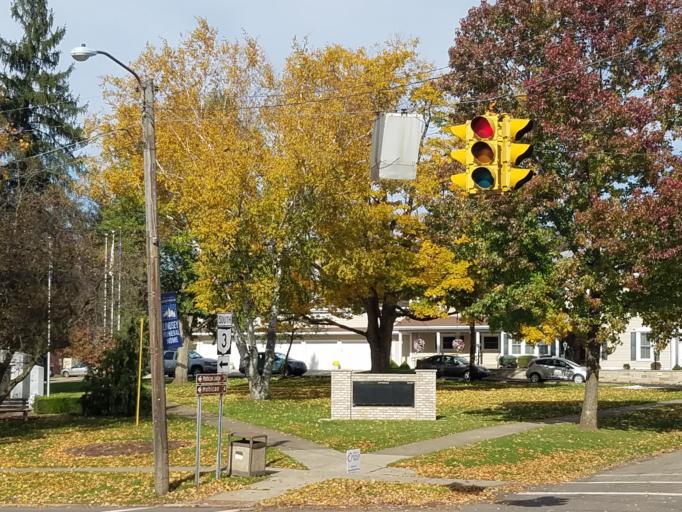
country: US
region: Ohio
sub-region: Ashland County
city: Loudonville
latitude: 40.6355
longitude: -82.2335
